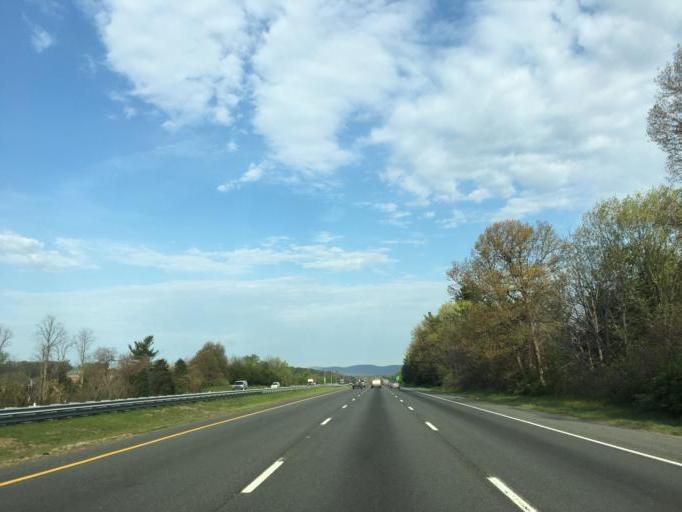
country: US
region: Maryland
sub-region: Frederick County
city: Spring Ridge
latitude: 39.3896
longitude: -77.3155
